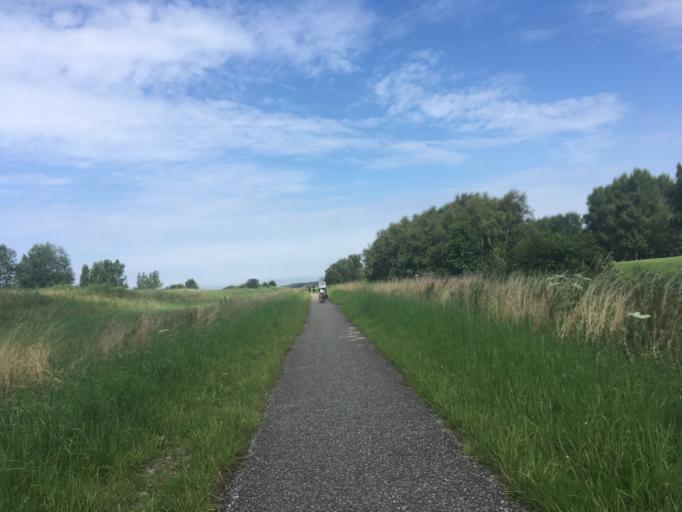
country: NL
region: North Holland
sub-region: Gemeente Haarlem
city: Haarlem
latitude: 52.4003
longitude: 4.7229
